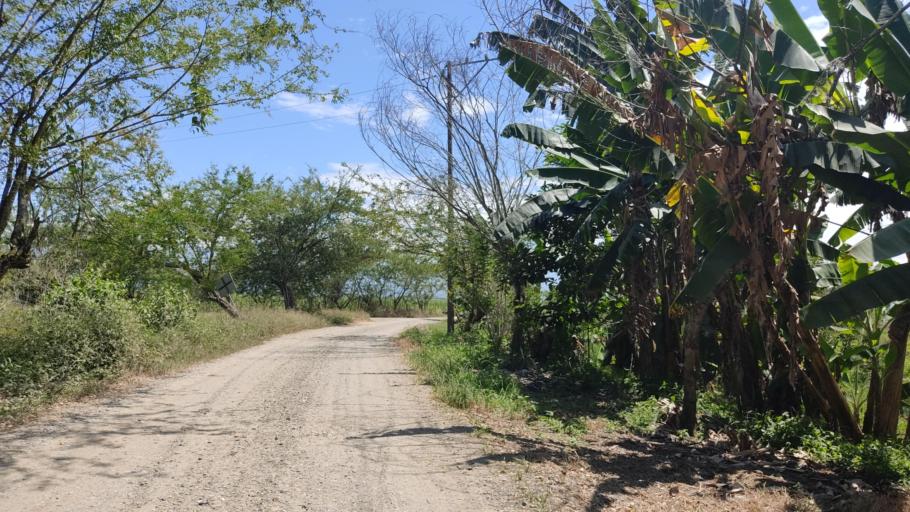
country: CO
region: Valle del Cauca
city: Jamundi
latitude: 3.1564
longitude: -76.5120
